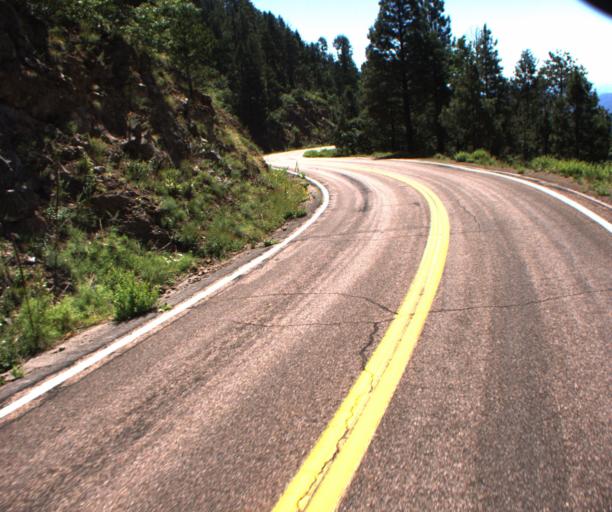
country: US
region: Arizona
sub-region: Greenlee County
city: Morenci
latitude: 33.5733
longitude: -109.3389
